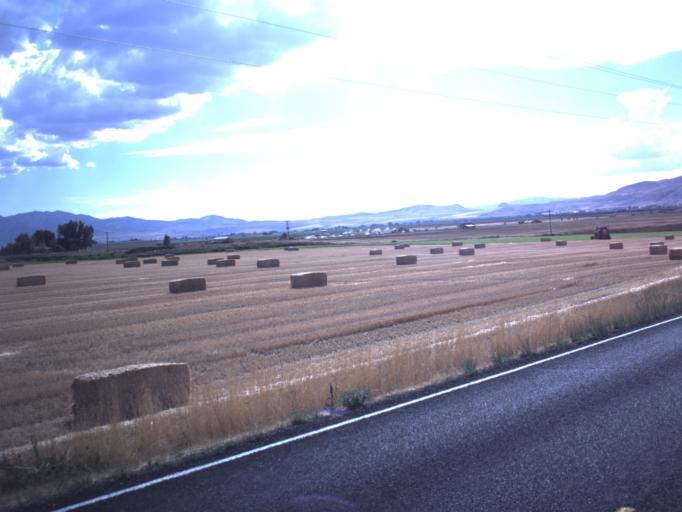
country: US
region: Utah
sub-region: Cache County
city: Richmond
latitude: 41.9229
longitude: -111.8258
